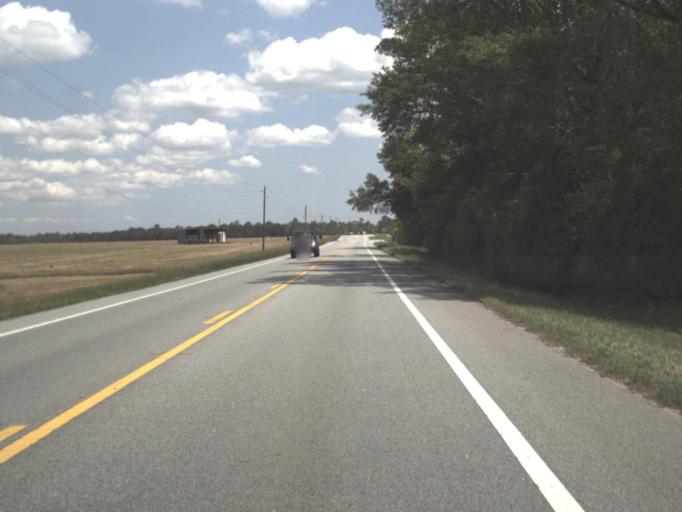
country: US
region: Florida
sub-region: Escambia County
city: Molino
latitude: 30.7449
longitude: -87.3668
